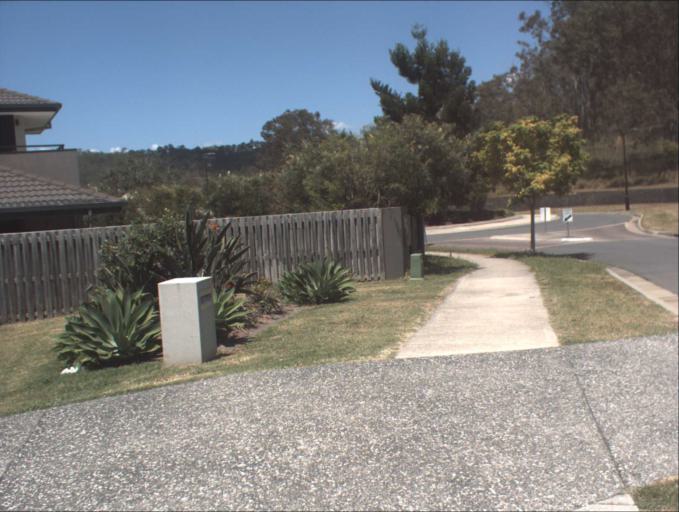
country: AU
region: Queensland
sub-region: Logan
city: Windaroo
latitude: -27.7503
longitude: 153.1821
